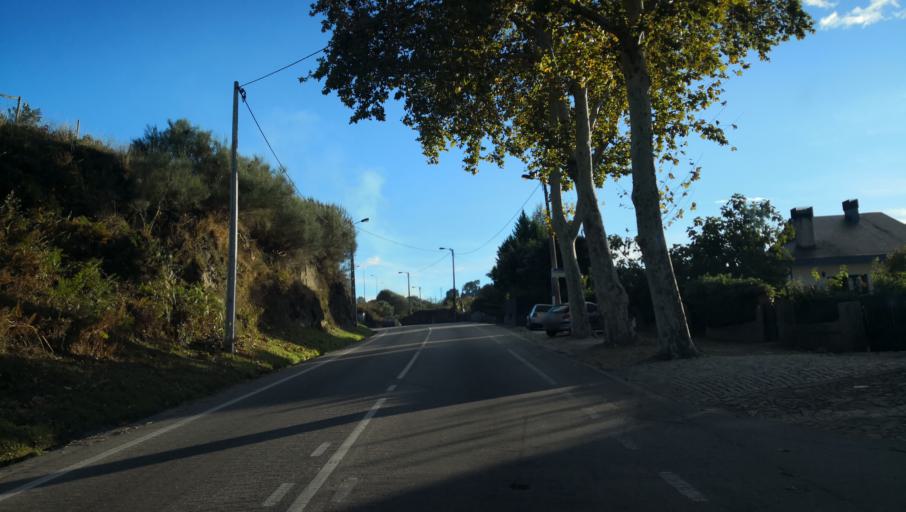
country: PT
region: Vila Real
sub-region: Vila Real
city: Vila Real
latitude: 41.2902
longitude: -7.7575
